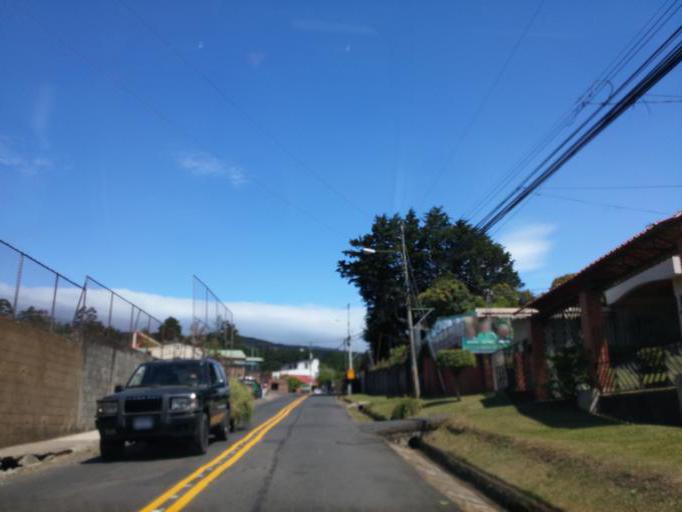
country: CR
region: Heredia
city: Santo Domingo
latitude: 10.0578
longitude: -84.1359
